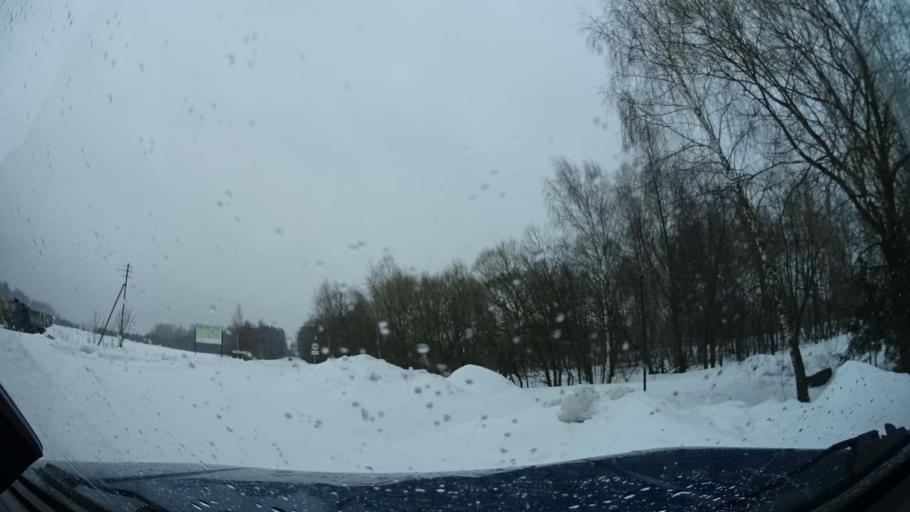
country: RU
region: Tverskaya
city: Konakovo
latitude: 56.7018
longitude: 36.6543
